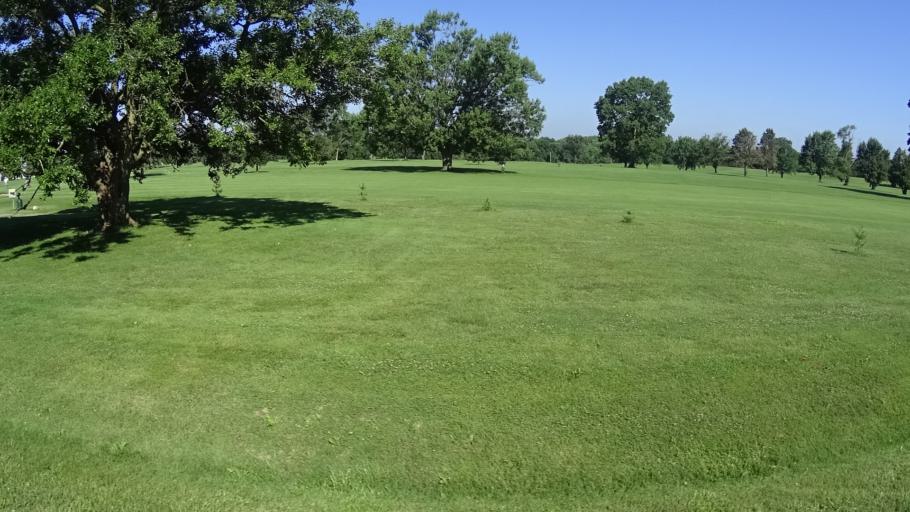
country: US
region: Indiana
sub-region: Madison County
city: Pendleton
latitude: 39.9862
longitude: -85.7537
